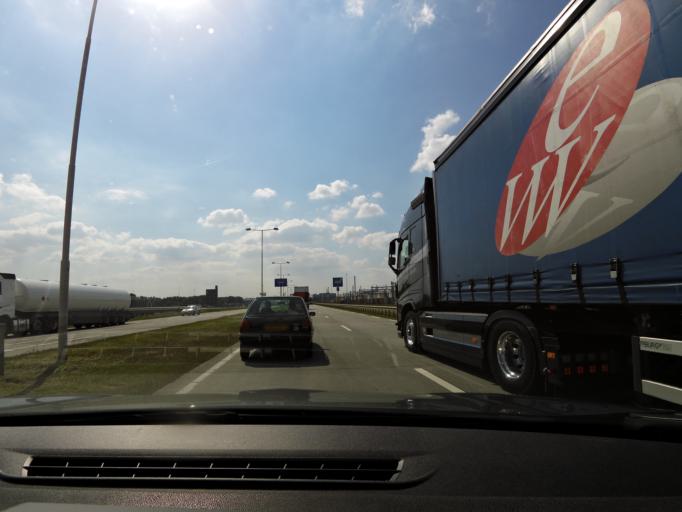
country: NL
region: South Holland
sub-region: Gemeente Schiedam
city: Schiedam
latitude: 51.8774
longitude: 4.3781
